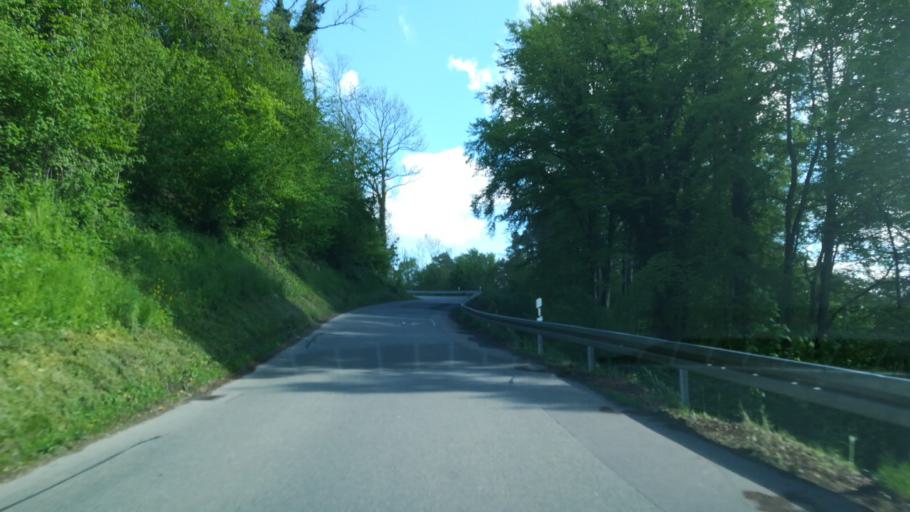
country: DE
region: Baden-Wuerttemberg
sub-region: Freiburg Region
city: Stuhlingen
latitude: 47.7436
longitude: 8.4373
